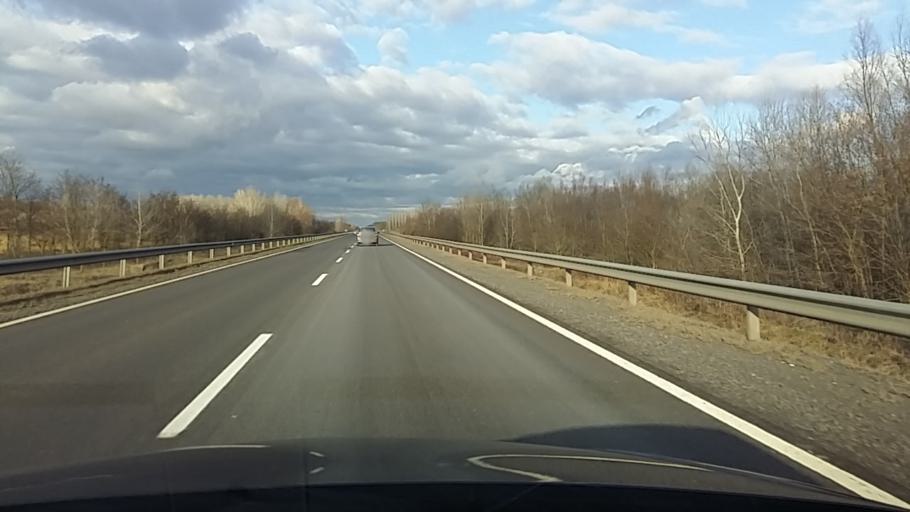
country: HU
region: Szabolcs-Szatmar-Bereg
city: Nagykallo
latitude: 47.9087
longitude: 21.8181
